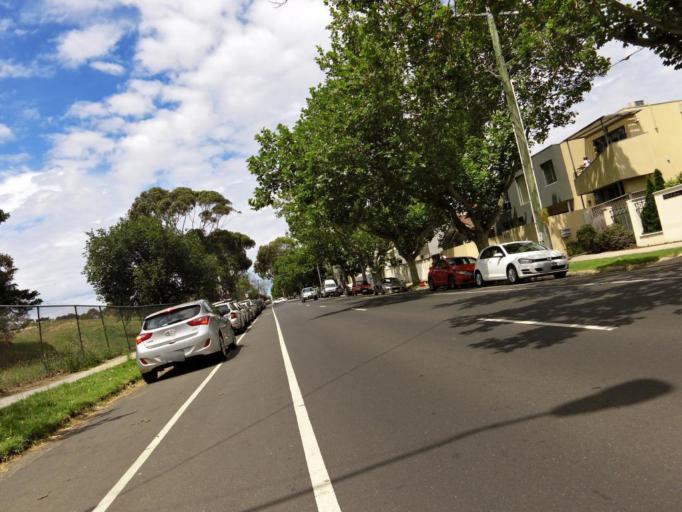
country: AU
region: Victoria
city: Ripponlea
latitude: -37.8864
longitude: 144.9917
